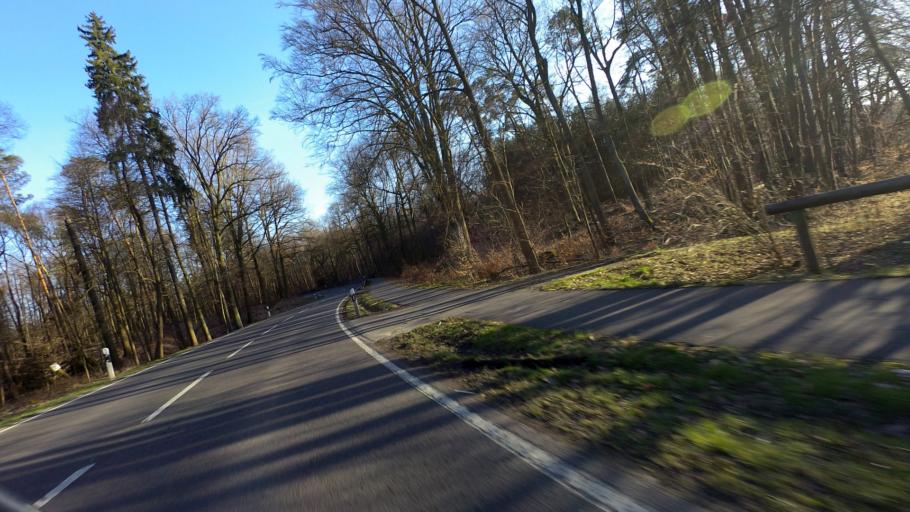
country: DE
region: Brandenburg
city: Britz
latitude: 52.8646
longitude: 13.8274
